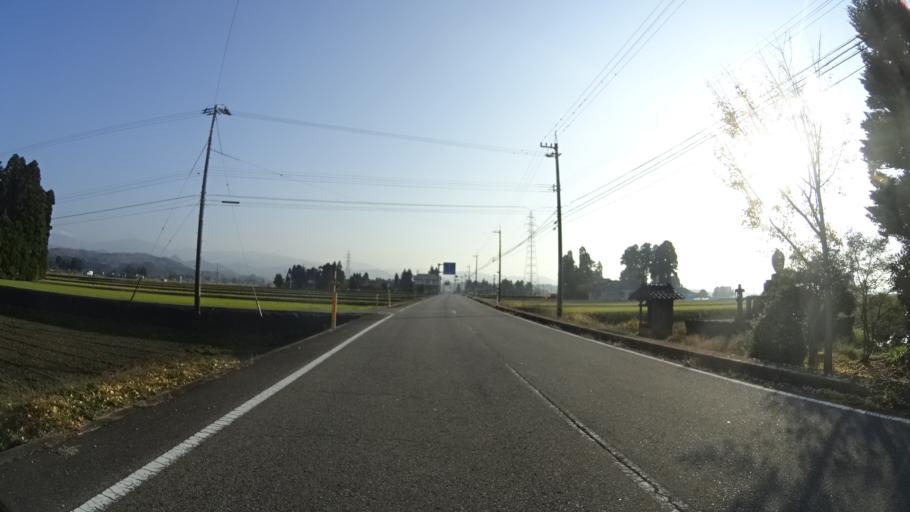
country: JP
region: Toyama
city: Kamiichi
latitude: 36.6271
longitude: 137.3158
